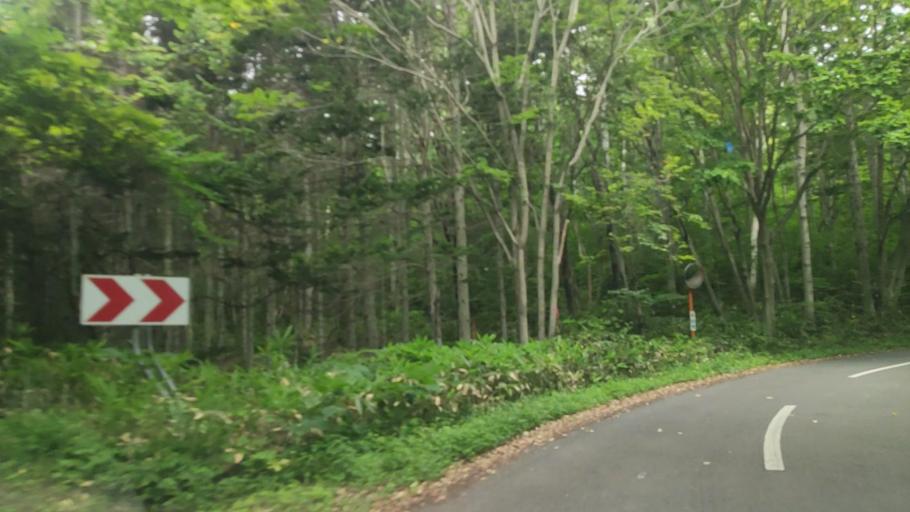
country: JP
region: Hokkaido
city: Otaru
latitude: 43.1955
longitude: 140.9807
